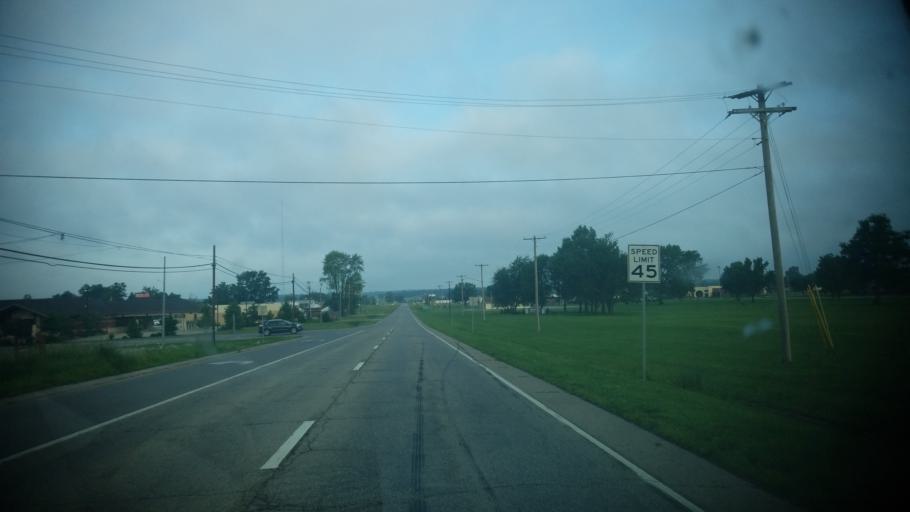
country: US
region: Illinois
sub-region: Wayne County
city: Fairfield
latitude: 38.3797
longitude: -88.3880
